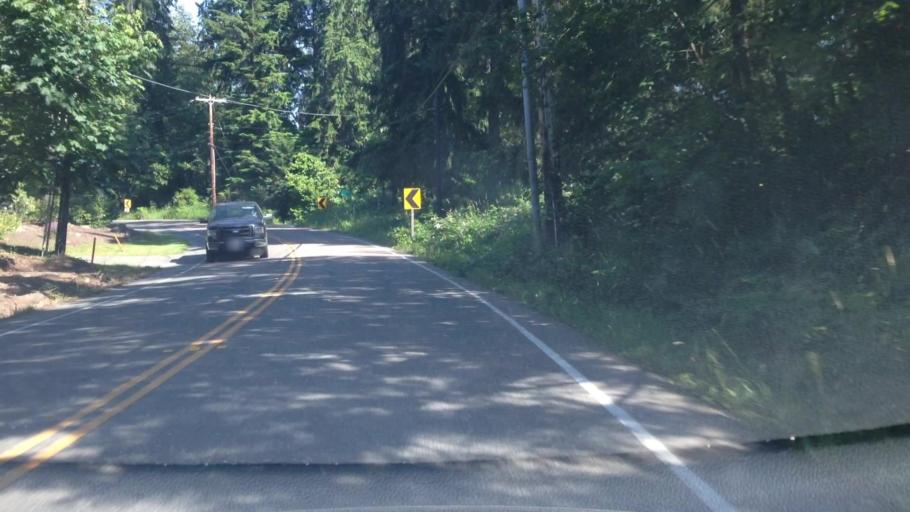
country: US
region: Washington
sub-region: King County
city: Lake Marcel-Stillwater
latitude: 47.7440
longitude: -121.9267
